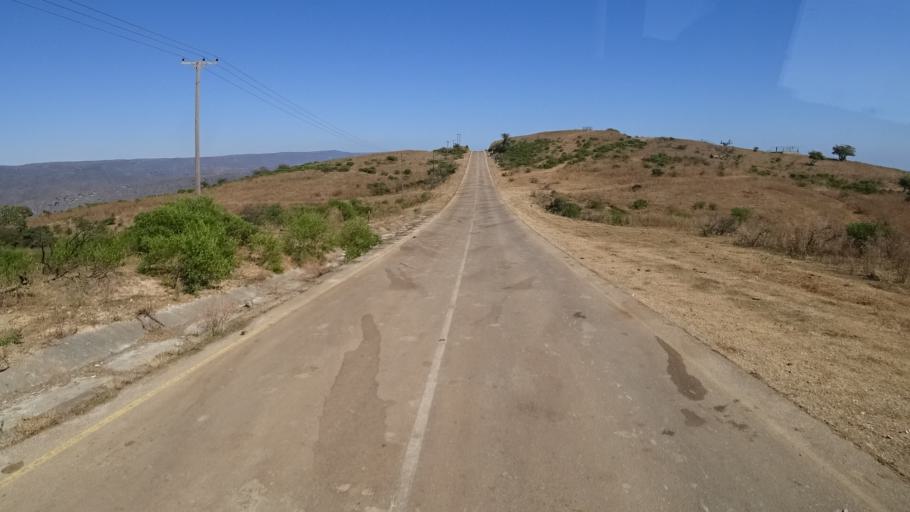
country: YE
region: Al Mahrah
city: Hawf
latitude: 16.7446
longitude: 53.3518
